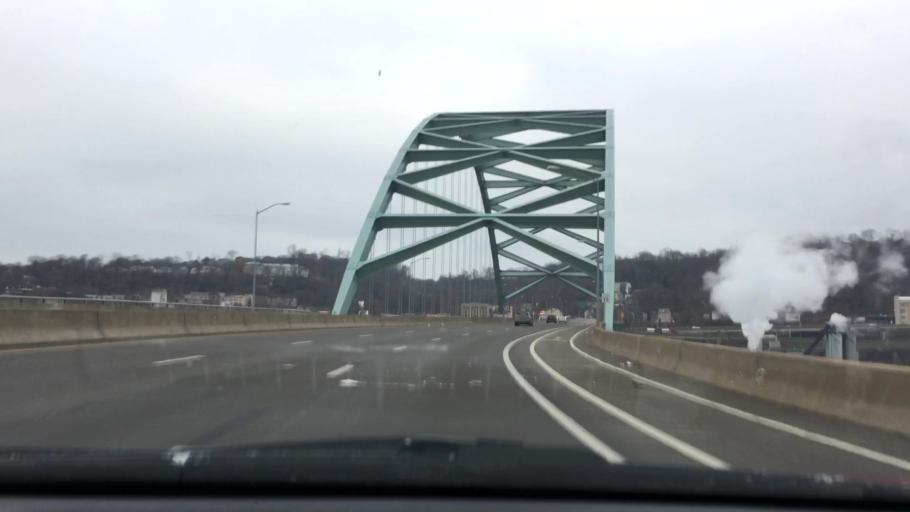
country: US
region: Pennsylvania
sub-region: Allegheny County
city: Mount Oliver
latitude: 40.4315
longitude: -79.9737
